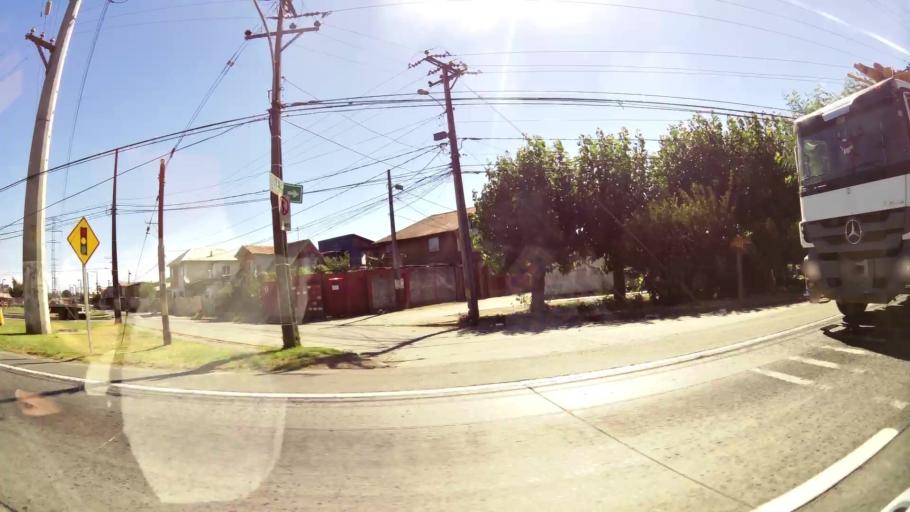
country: CL
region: Biobio
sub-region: Provincia de Concepcion
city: Concepcion
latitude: -36.7967
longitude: -73.0258
